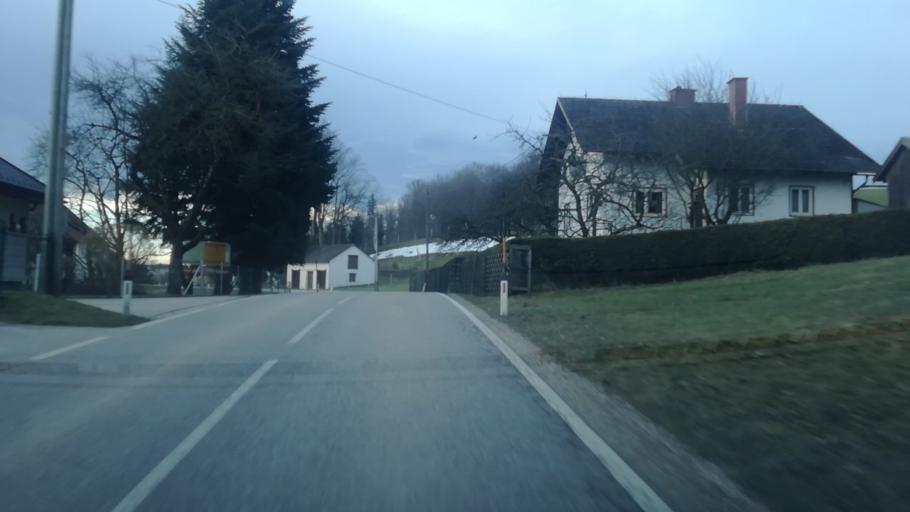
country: AT
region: Upper Austria
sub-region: Politischer Bezirk Ried im Innkreis
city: Waldzell
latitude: 48.1799
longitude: 13.4435
